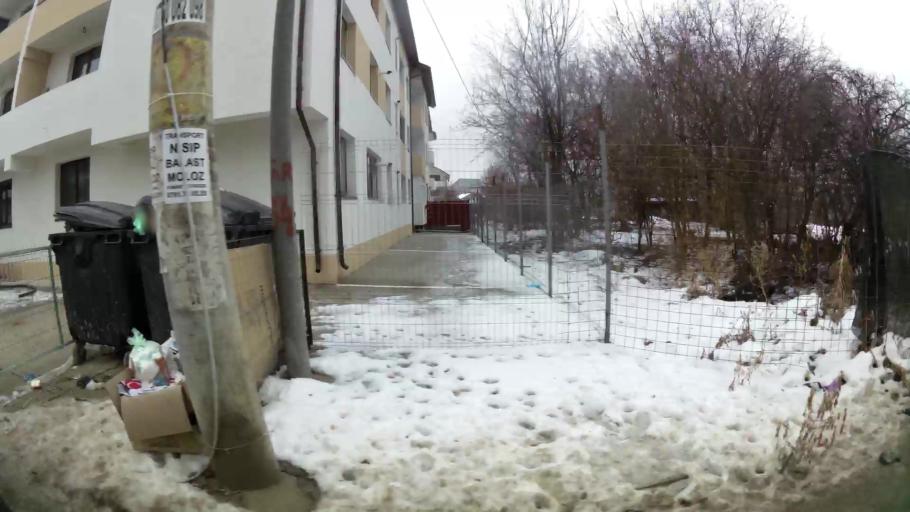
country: RO
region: Ilfov
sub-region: Comuna Popesti-Leordeni
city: Popesti-Leordeni
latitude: 44.4056
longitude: 26.1663
